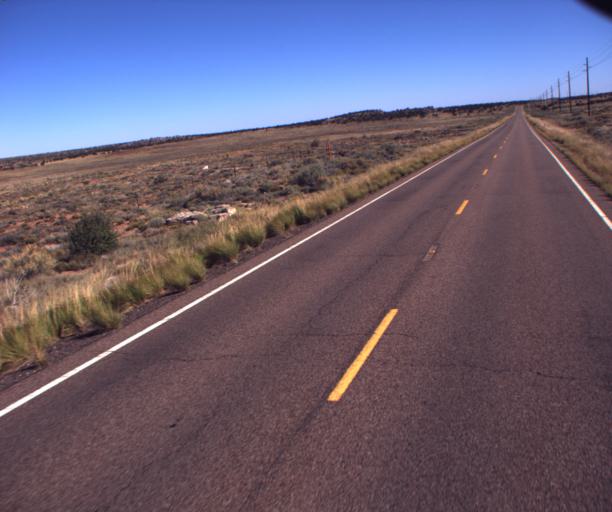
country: US
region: Arizona
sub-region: Navajo County
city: Taylor
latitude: 34.5014
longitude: -110.1939
